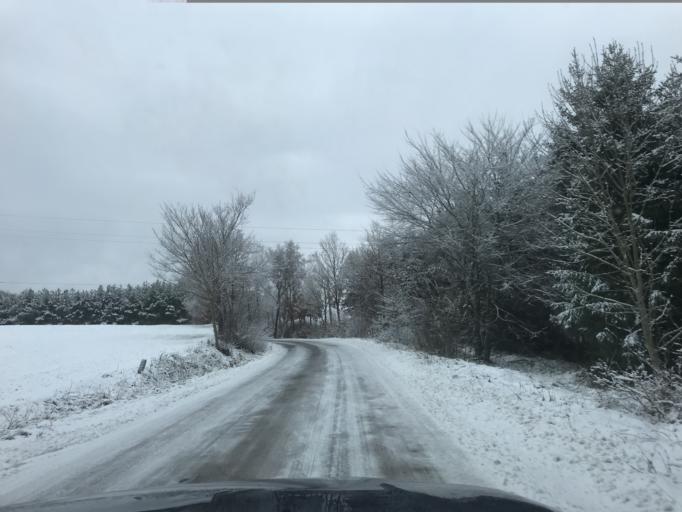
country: PL
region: Pomeranian Voivodeship
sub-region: Powiat bytowski
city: Parchowo
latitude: 54.2348
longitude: 17.5746
